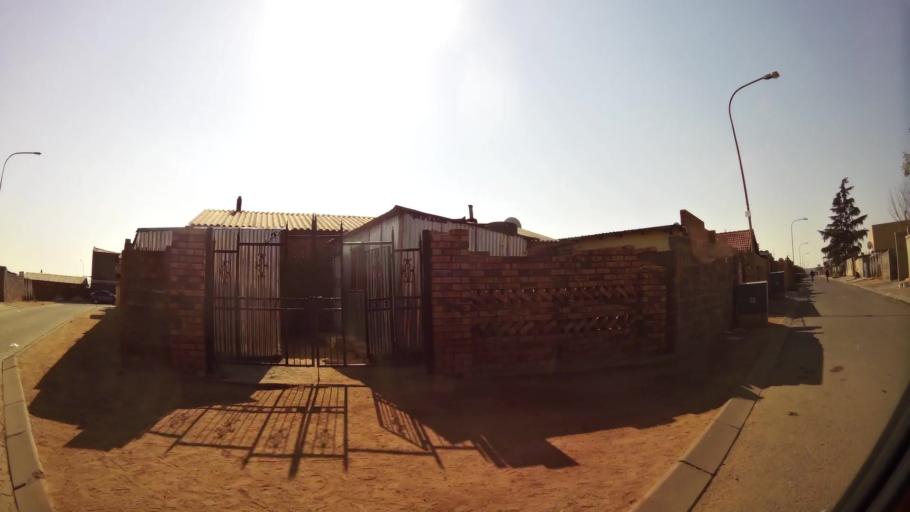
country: ZA
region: Gauteng
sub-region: City of Johannesburg Metropolitan Municipality
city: Soweto
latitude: -26.2441
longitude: 27.9430
